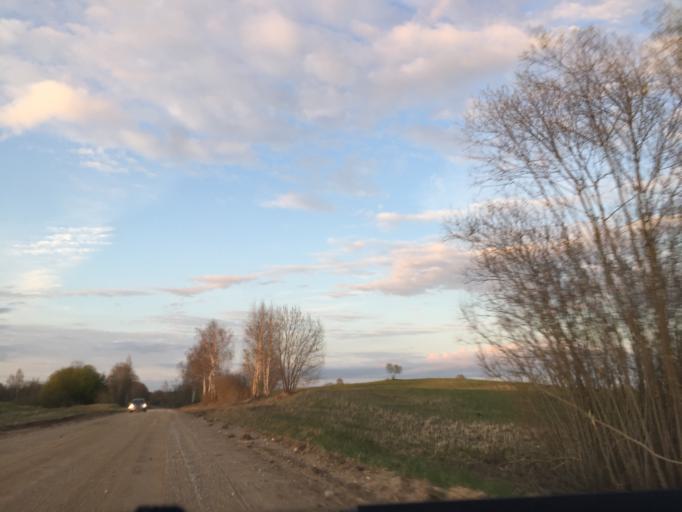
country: LV
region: Gulbenes Rajons
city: Gulbene
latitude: 57.2349
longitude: 26.8088
